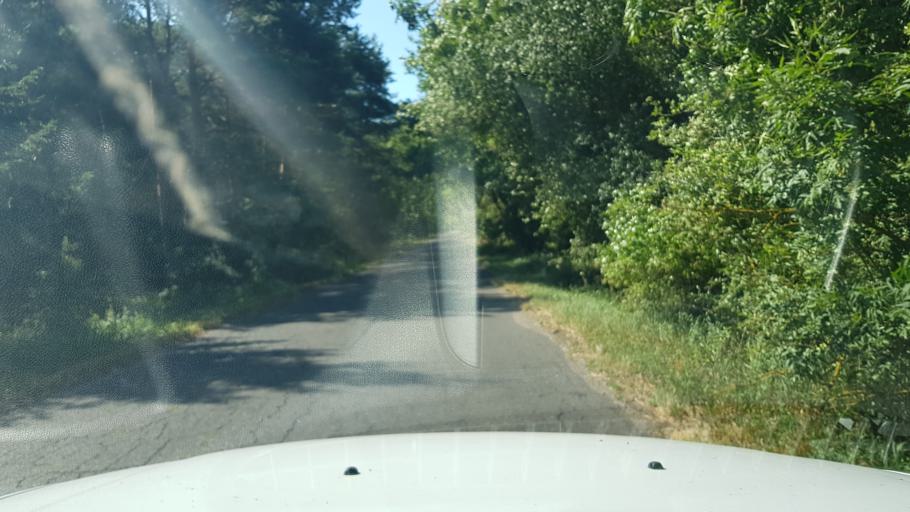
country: PL
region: West Pomeranian Voivodeship
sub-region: Powiat goleniowski
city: Goleniow
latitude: 53.4842
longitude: 14.7116
